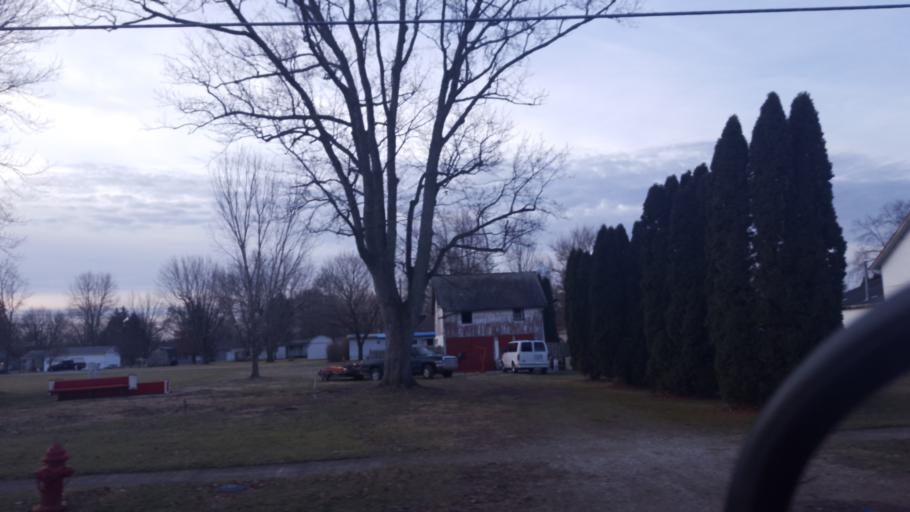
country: US
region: Ohio
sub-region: Morrow County
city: Cardington
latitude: 40.5003
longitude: -82.9031
